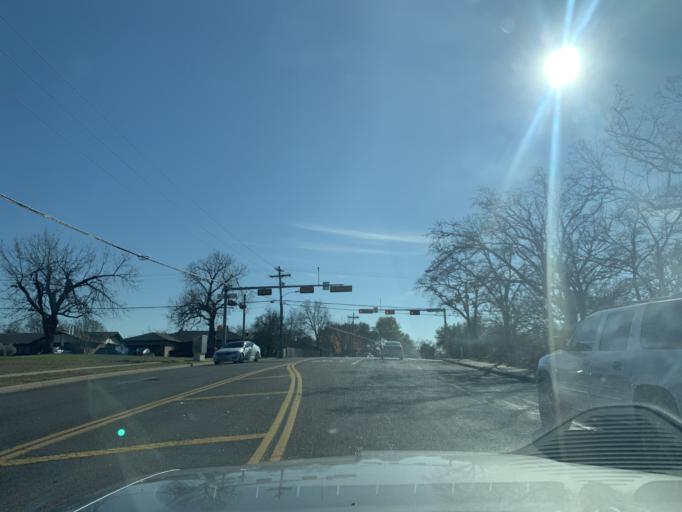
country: US
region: Texas
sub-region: Tarrant County
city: Bedford
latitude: 32.8313
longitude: -97.1425
